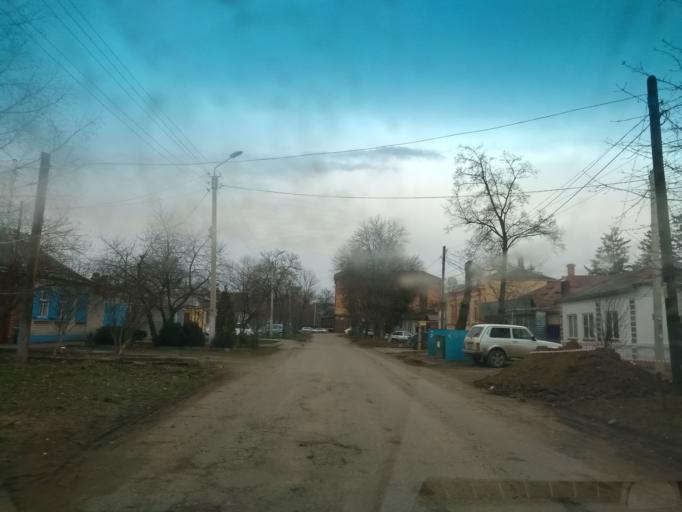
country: RU
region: Stavropol'skiy
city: Georgiyevsk
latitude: 44.1494
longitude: 43.4675
